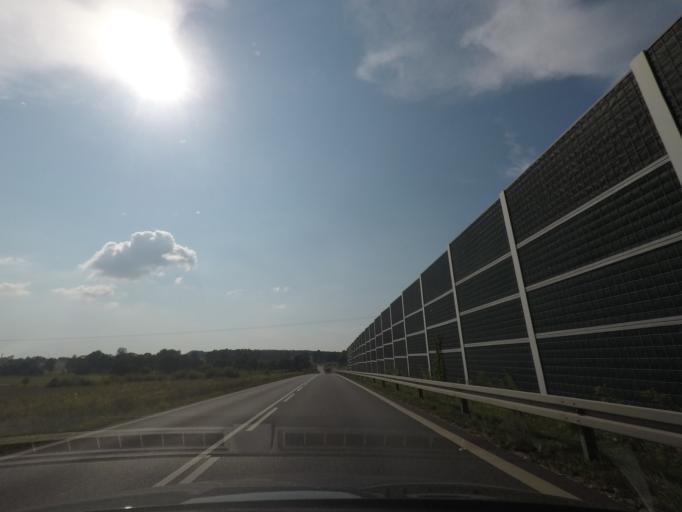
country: PL
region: Silesian Voivodeship
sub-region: Powiat pszczynski
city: Czarkow
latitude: 50.0018
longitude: 18.9159
